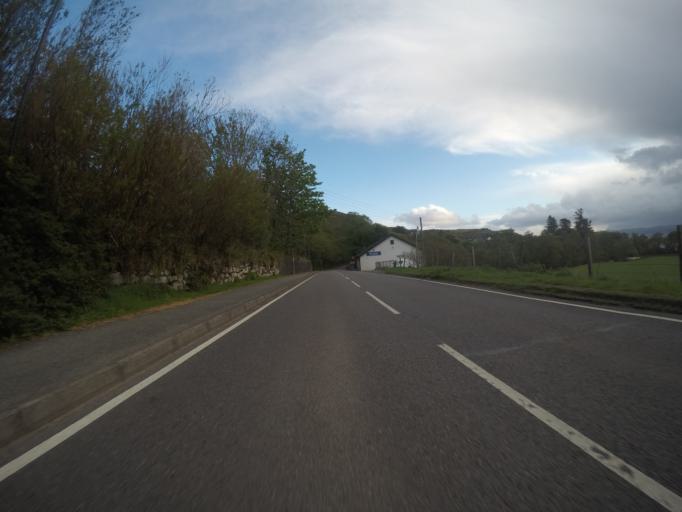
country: GB
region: Scotland
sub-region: Highland
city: Portree
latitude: 57.5905
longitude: -6.3552
